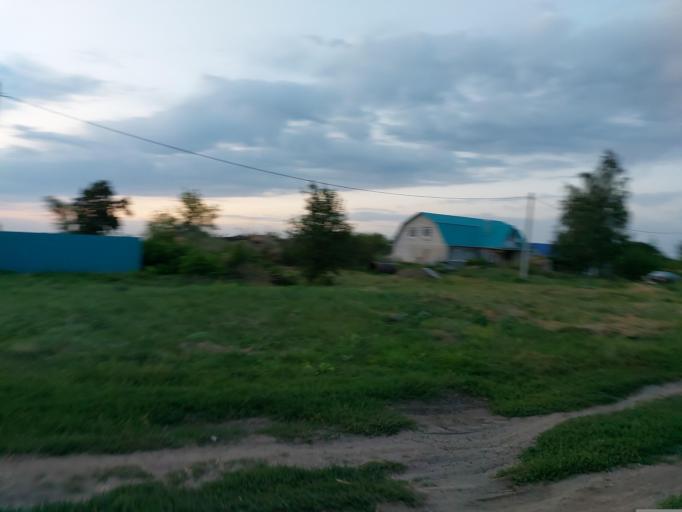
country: RU
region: Lipetsk
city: Dolgorukovo
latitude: 52.3779
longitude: 38.0497
